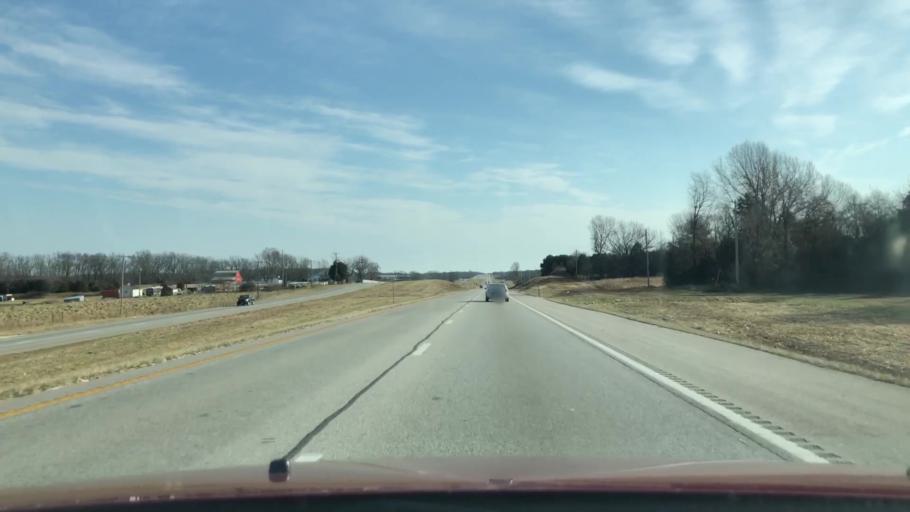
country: US
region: Missouri
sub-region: Webster County
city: Rogersville
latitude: 37.1195
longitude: -93.1630
